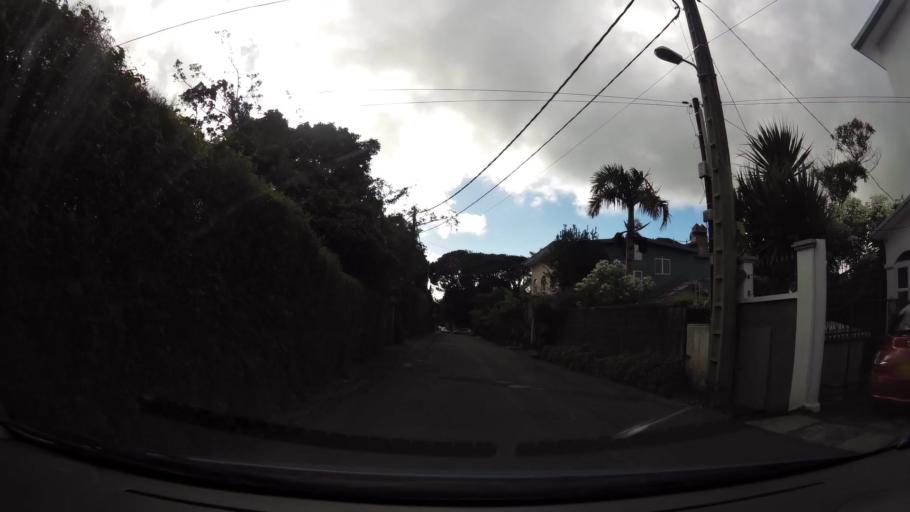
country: MU
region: Plaines Wilhems
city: Curepipe
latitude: -20.3252
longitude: 57.5220
